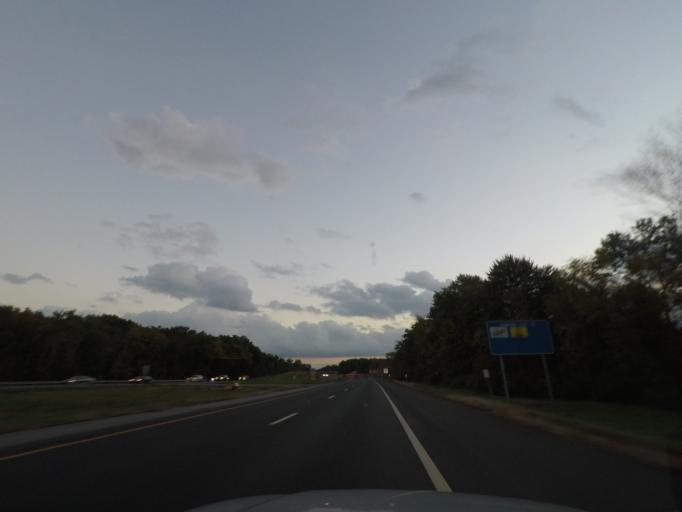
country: US
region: New York
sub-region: Ulster County
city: New Paltz
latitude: 41.7486
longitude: -74.0628
